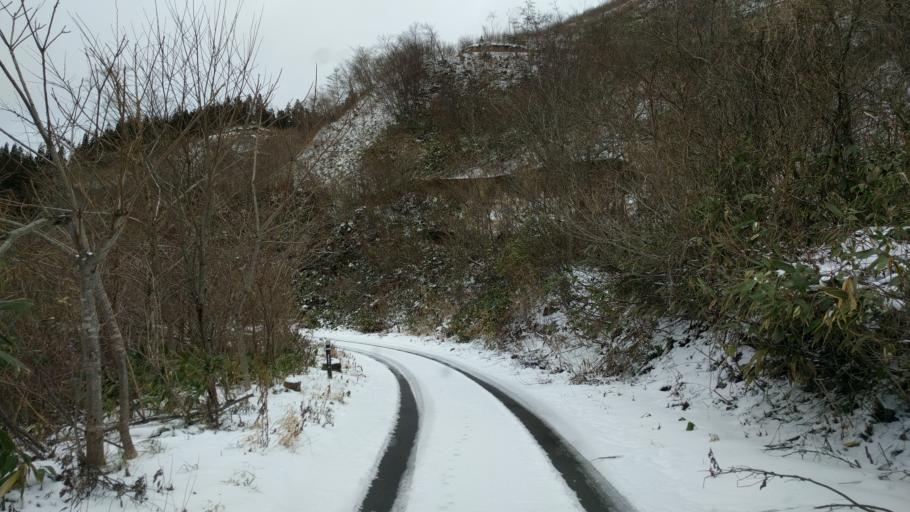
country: JP
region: Fukushima
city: Inawashiro
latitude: 37.3807
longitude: 140.0226
